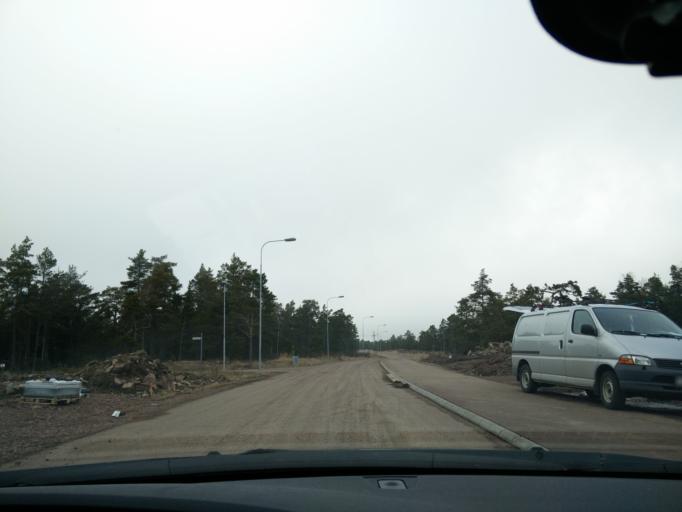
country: AX
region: Mariehamns stad
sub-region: Mariehamn
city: Mariehamn
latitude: 60.1249
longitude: 19.9294
